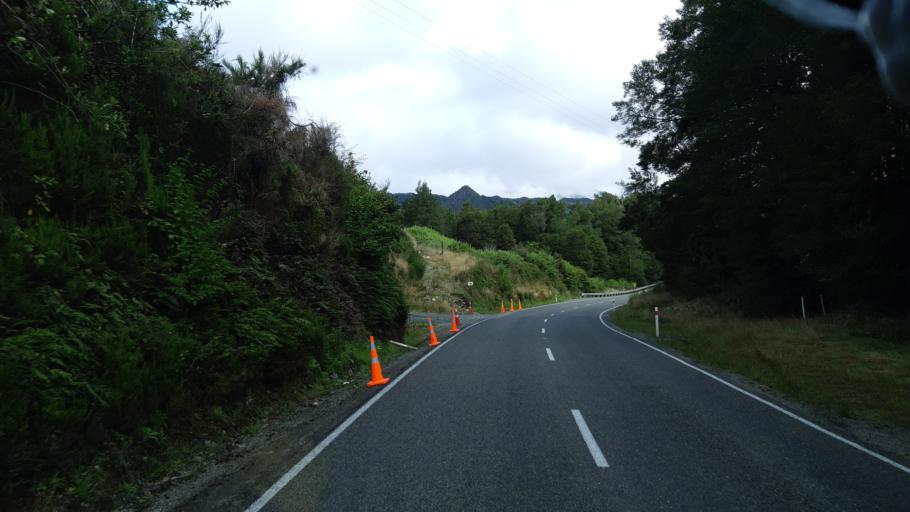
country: NZ
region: West Coast
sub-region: Buller District
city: Westport
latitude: -41.9842
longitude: 172.2061
